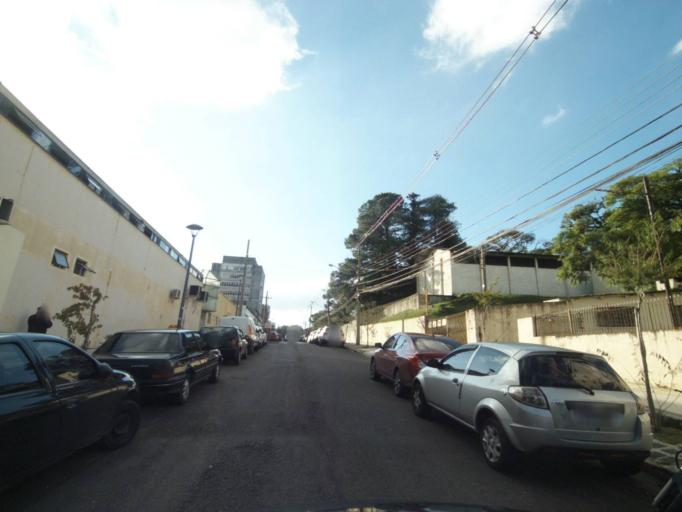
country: BR
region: Parana
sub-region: Curitiba
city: Curitiba
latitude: -25.4240
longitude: -49.2615
